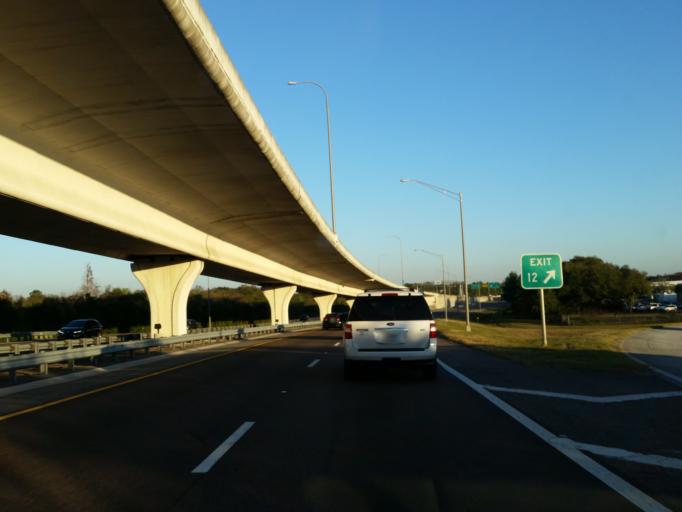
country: US
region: Florida
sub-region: Hillsborough County
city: Palm River-Clair Mel
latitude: 27.9495
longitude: -82.3680
